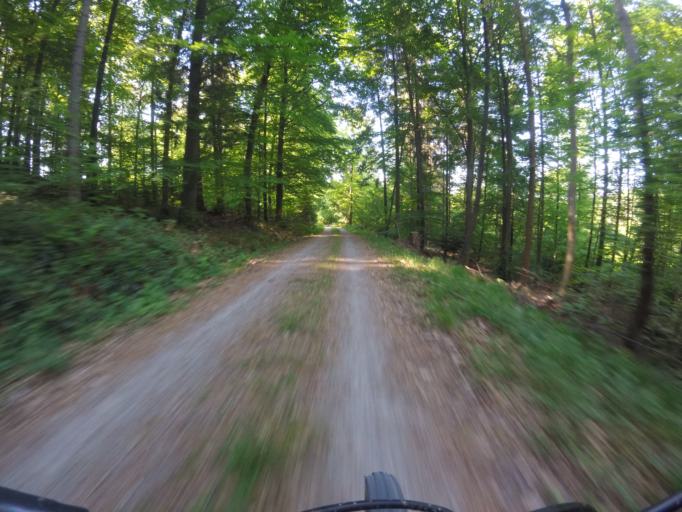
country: DE
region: Baden-Wuerttemberg
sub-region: Regierungsbezirk Stuttgart
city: Aspach
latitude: 49.0080
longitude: 9.4095
